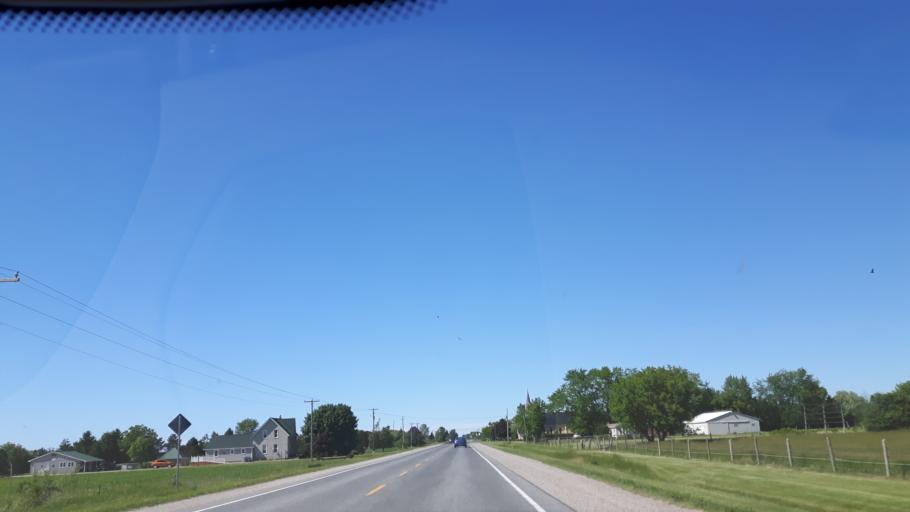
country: CA
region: Ontario
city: Bluewater
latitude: 43.4336
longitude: -81.7035
